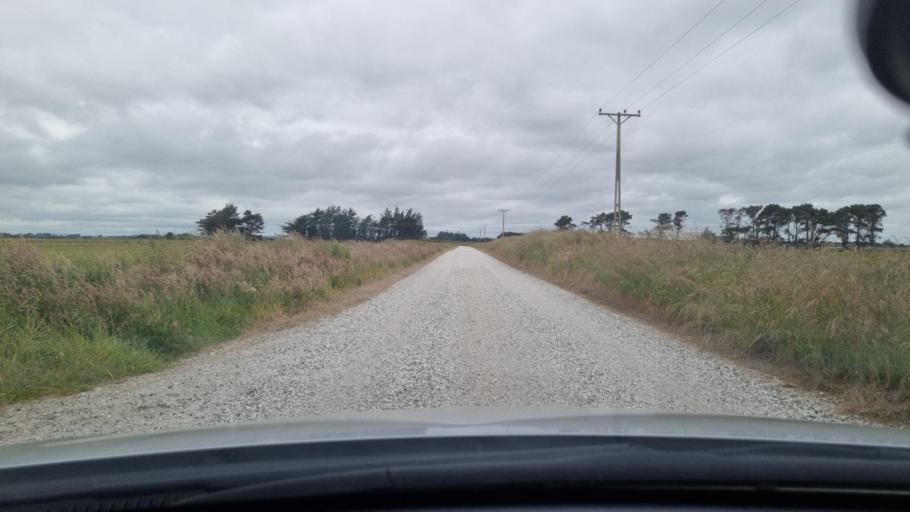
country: NZ
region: Southland
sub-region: Invercargill City
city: Invercargill
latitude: -46.3888
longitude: 168.2782
